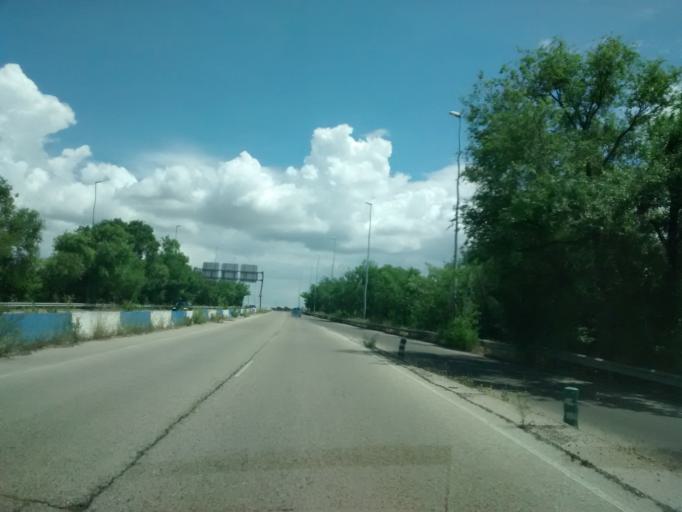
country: ES
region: Madrid
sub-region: Provincia de Madrid
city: Coslada
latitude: 40.4336
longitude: -3.5565
